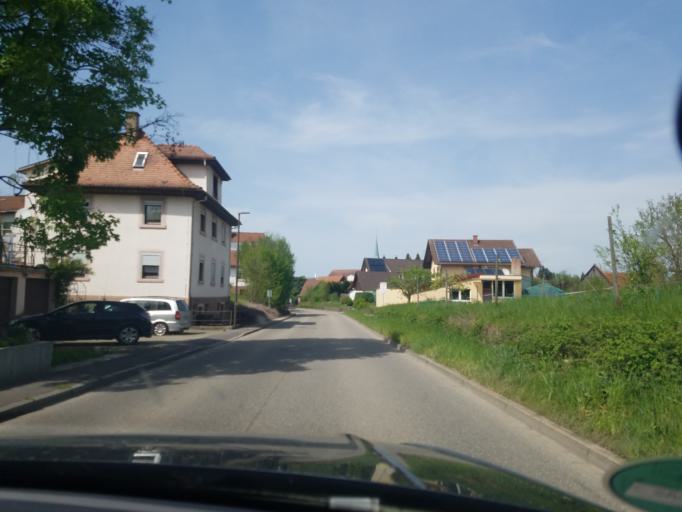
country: DE
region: Baden-Wuerttemberg
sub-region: Freiburg Region
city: Haslach
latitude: 48.5768
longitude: 8.0503
